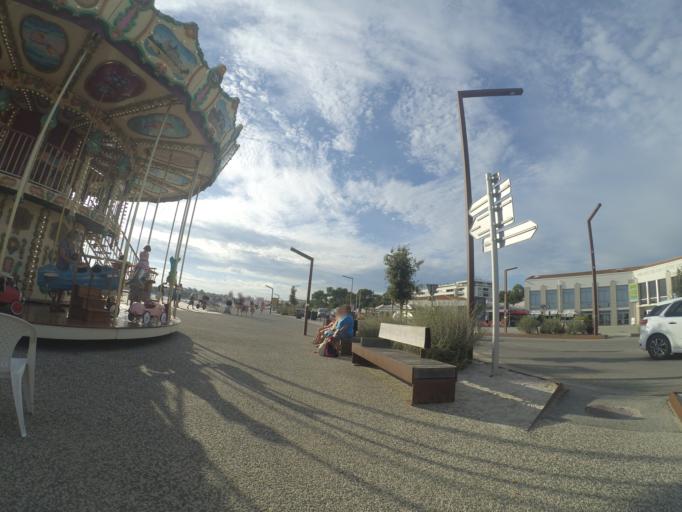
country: FR
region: Poitou-Charentes
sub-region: Departement de la Charente-Maritime
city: Saint-Georges-de-Didonne
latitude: 45.5988
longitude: -0.9937
